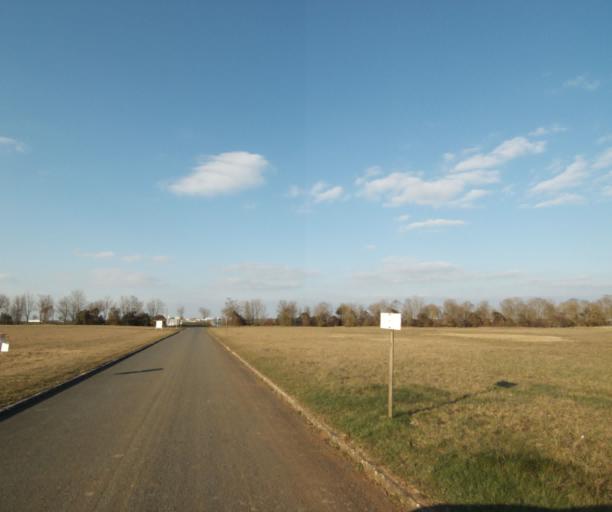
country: FR
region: Poitou-Charentes
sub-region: Departement des Deux-Sevres
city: Vouille
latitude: 46.3169
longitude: -0.3993
